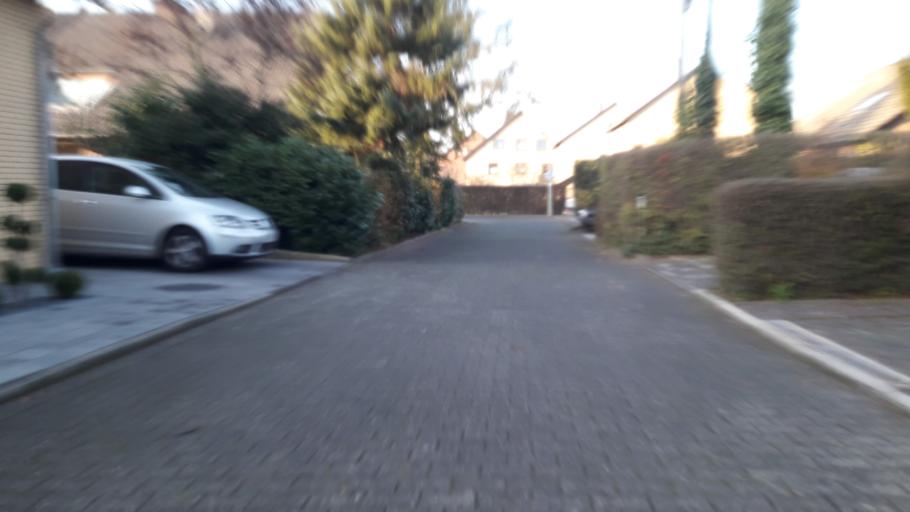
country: DE
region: North Rhine-Westphalia
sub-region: Regierungsbezirk Detmold
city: Paderborn
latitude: 51.7258
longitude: 8.7866
